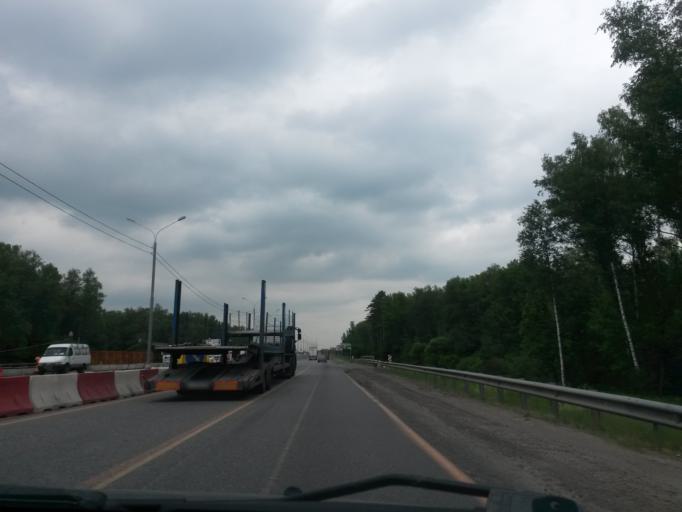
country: RU
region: Moskovskaya
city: Lyubuchany
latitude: 55.1963
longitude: 37.5350
